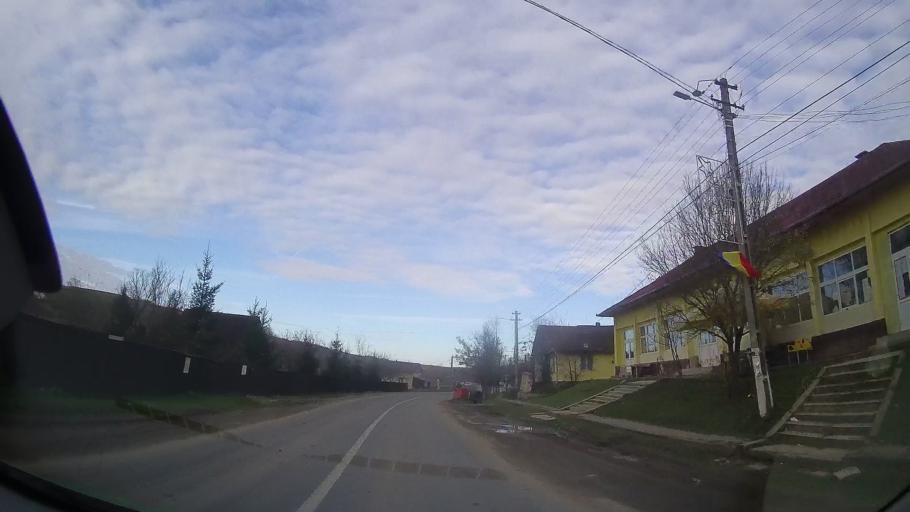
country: RO
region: Cluj
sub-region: Comuna Geaca
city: Geaca
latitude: 46.8556
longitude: 24.0893
